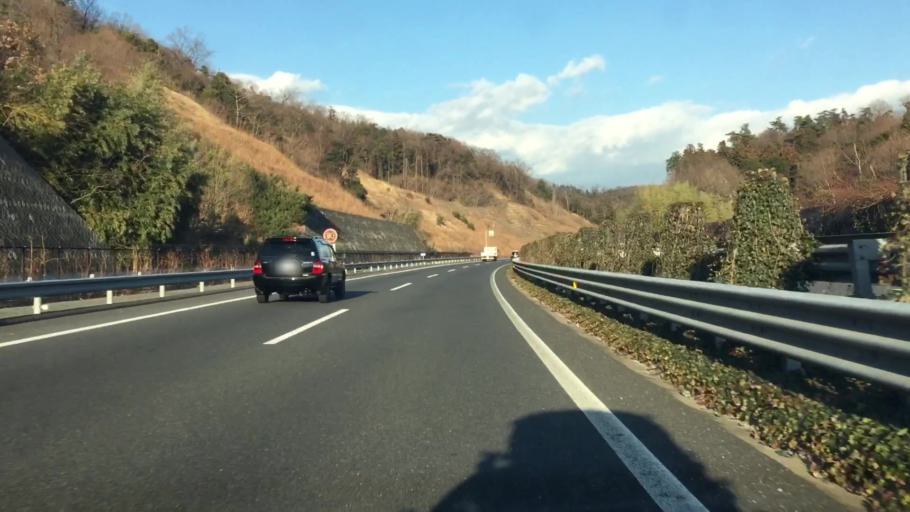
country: JP
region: Tochigi
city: Ashikaga
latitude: 36.3560
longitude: 139.4241
